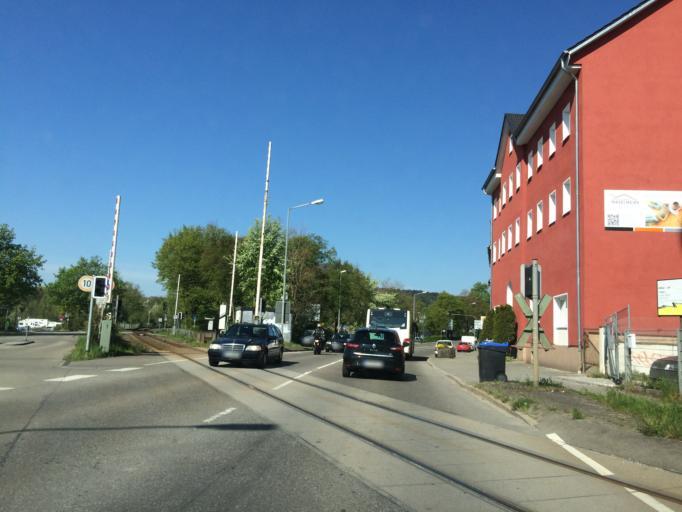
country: DE
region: Baden-Wuerttemberg
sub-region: Freiburg Region
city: Tuttlingen
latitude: 47.9861
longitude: 8.8153
